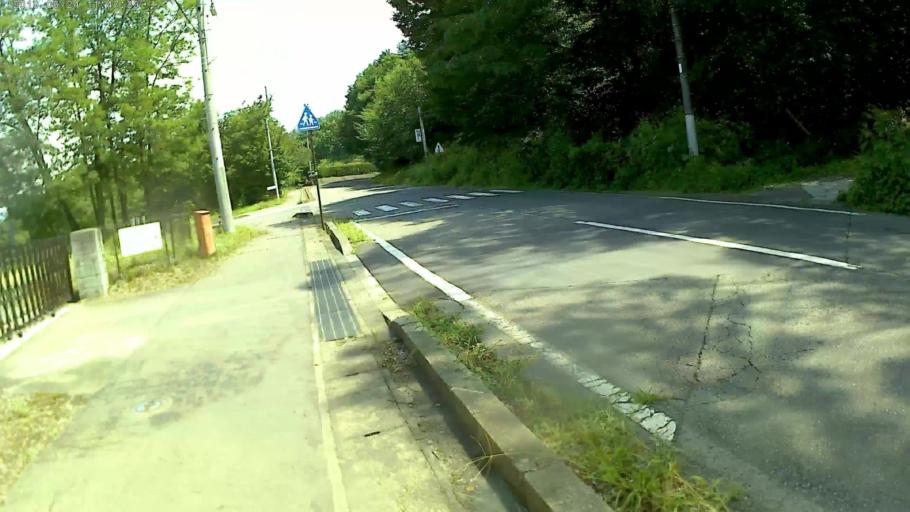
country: JP
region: Nagano
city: Kamimaruko
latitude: 36.2717
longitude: 138.3457
